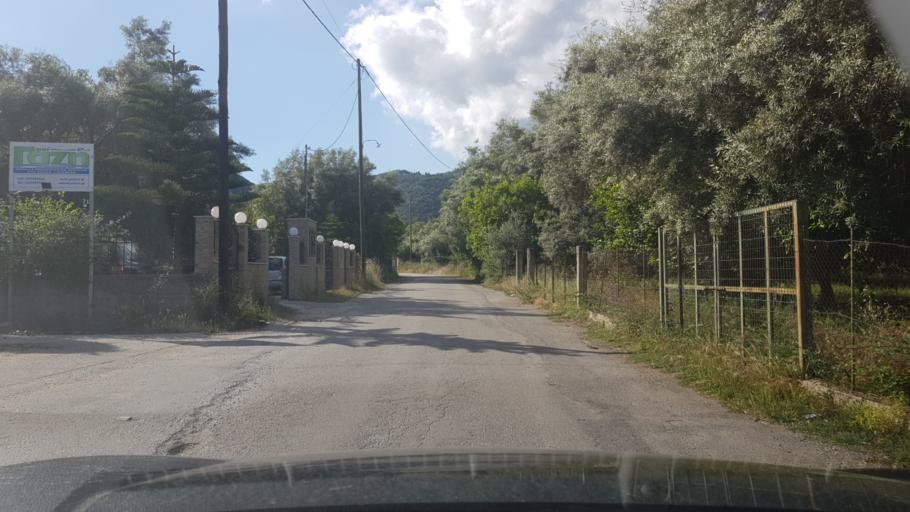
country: GR
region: Ionian Islands
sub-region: Lefkada
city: Nidri
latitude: 38.7128
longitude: 20.7030
